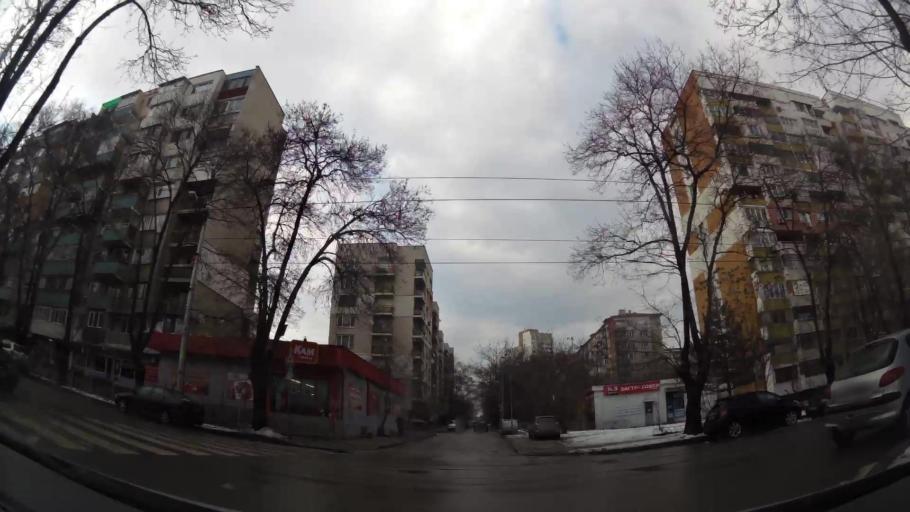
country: BG
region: Sofia-Capital
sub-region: Stolichna Obshtina
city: Sofia
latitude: 42.7077
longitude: 23.2898
